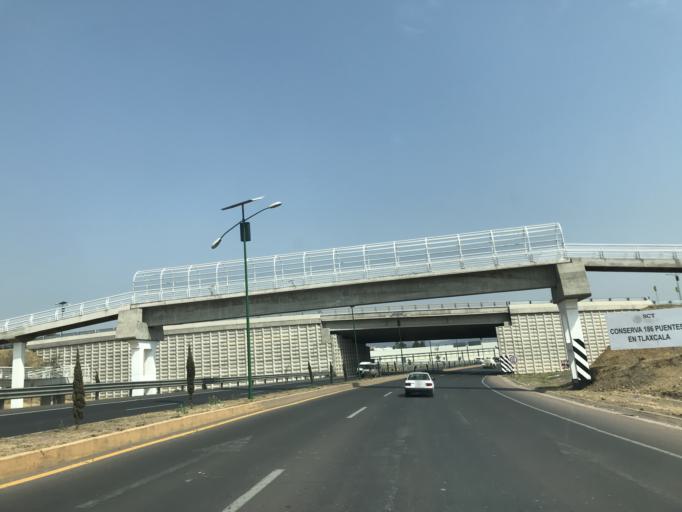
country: MX
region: Tlaxcala
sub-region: Chiautempan
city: Santa Cruz Tetela
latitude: 19.3031
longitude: -98.1986
